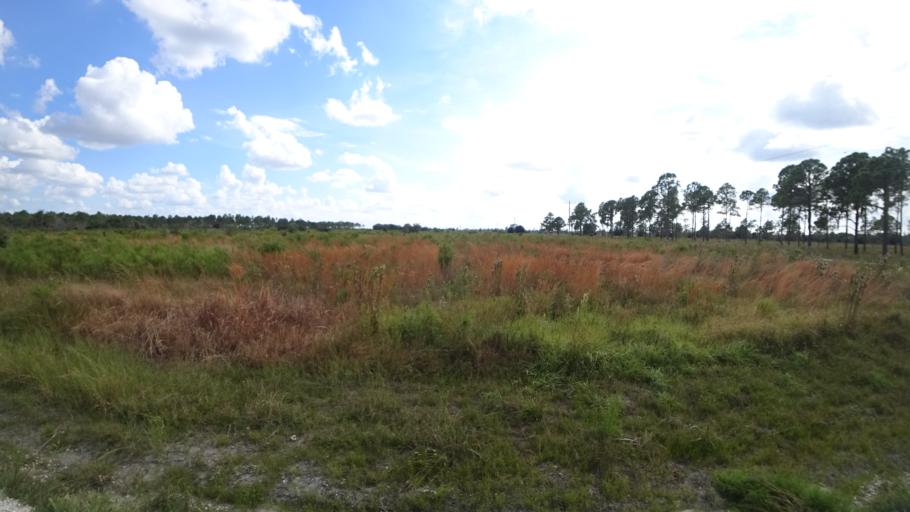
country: US
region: Florida
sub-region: Hillsborough County
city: Wimauma
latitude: 27.5420
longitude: -82.1276
